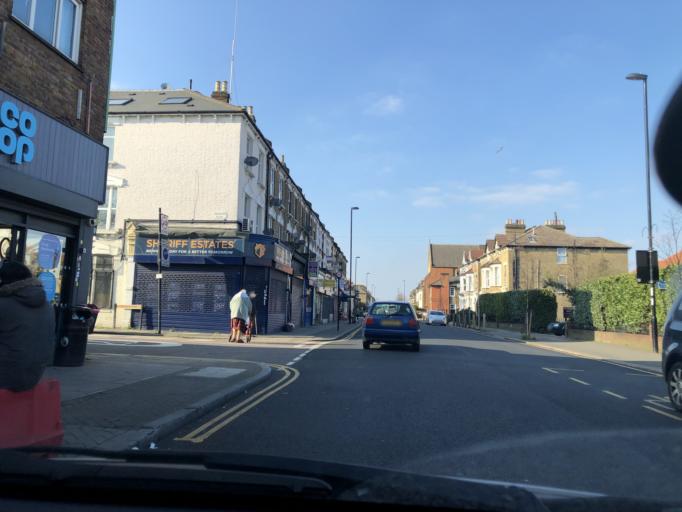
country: GB
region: England
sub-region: Greater London
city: Catford
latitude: 51.4511
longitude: -0.0063
